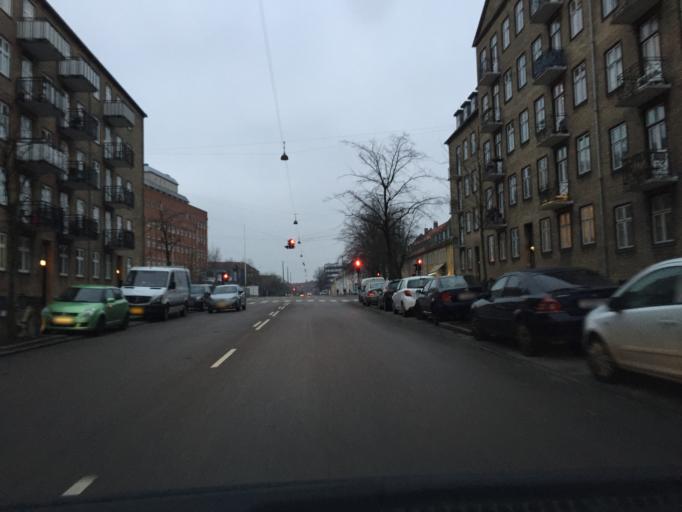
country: DK
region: Capital Region
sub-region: Frederiksberg Kommune
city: Frederiksberg
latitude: 55.7055
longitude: 12.5522
